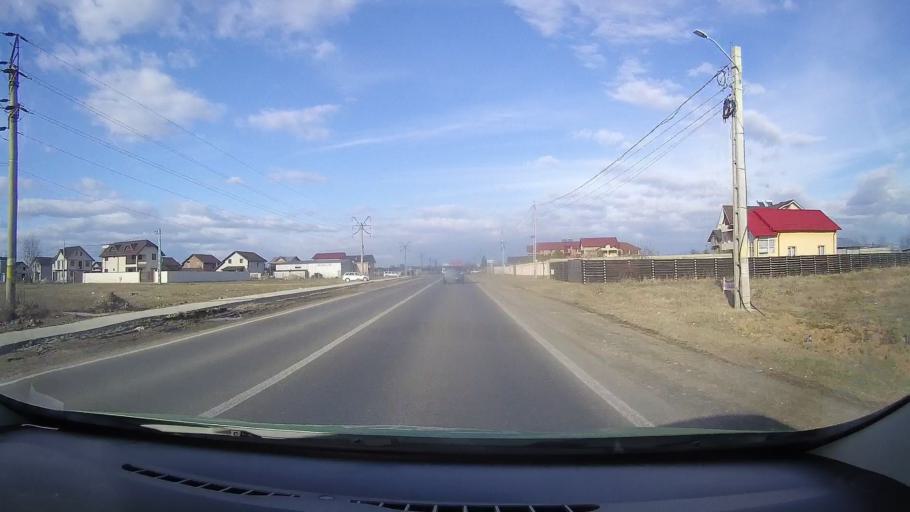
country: RO
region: Dambovita
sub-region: Comuna Ulmi
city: Viisoara
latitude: 44.8848
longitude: 25.4314
